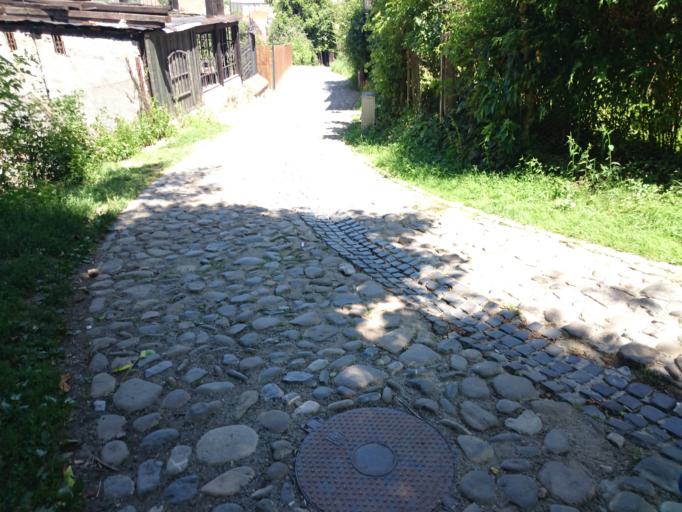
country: RO
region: Mures
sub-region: Municipiul Sighisoara
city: Sighisoara
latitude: 46.2185
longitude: 24.7903
